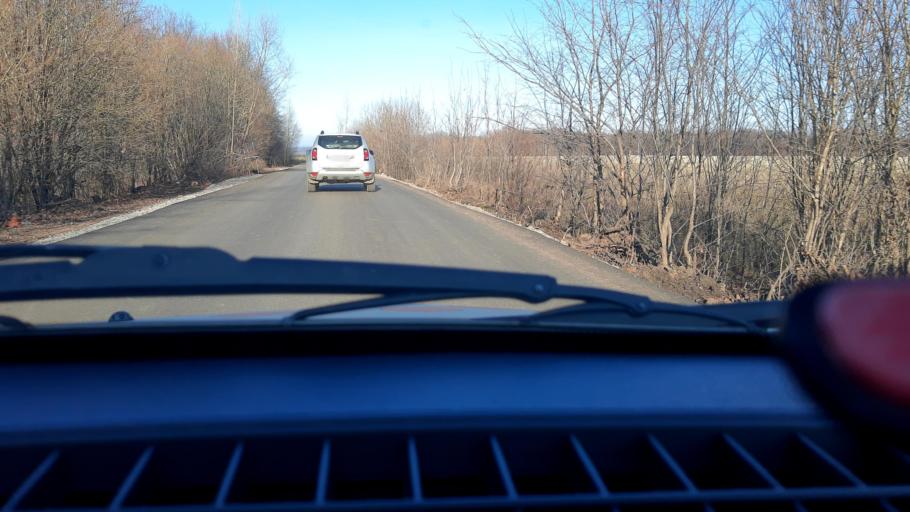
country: RU
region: Bashkortostan
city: Kabakovo
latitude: 54.6176
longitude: 56.1530
